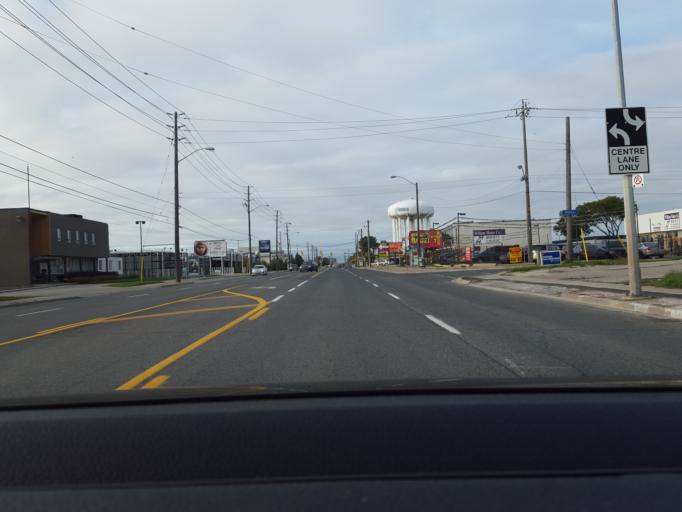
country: CA
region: Ontario
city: Scarborough
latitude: 43.7229
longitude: -79.2855
